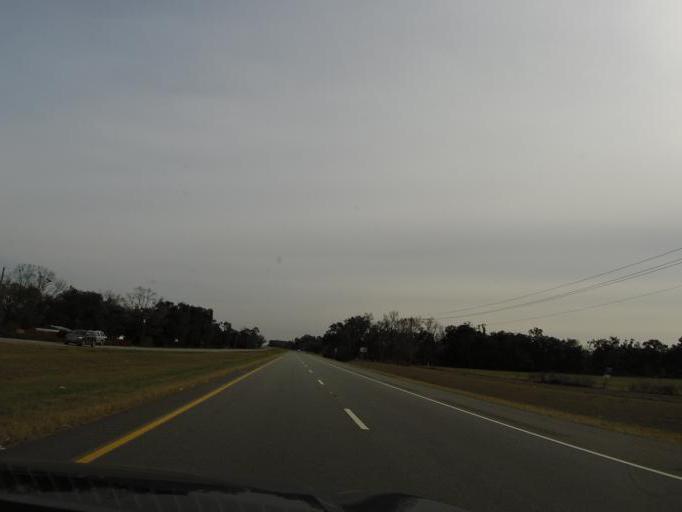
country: US
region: Georgia
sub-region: Seminole County
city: Donalsonville
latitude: 31.0892
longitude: -84.9912
